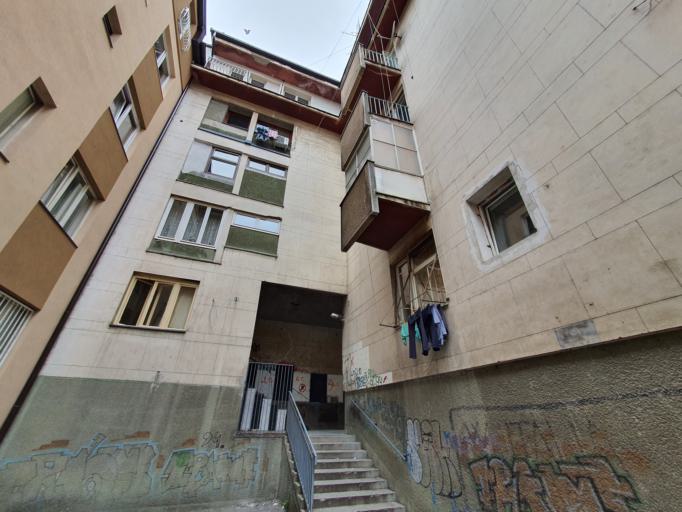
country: RS
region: Central Serbia
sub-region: Zlatiborski Okrug
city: Uzice
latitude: 43.8562
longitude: 19.8415
